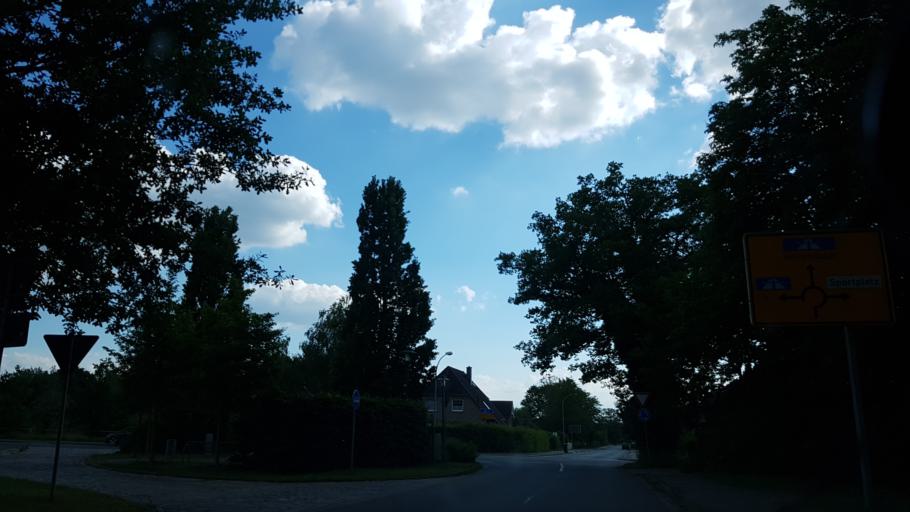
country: DE
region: Lower Saxony
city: Wenzendorf
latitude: 53.3520
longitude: 9.7693
